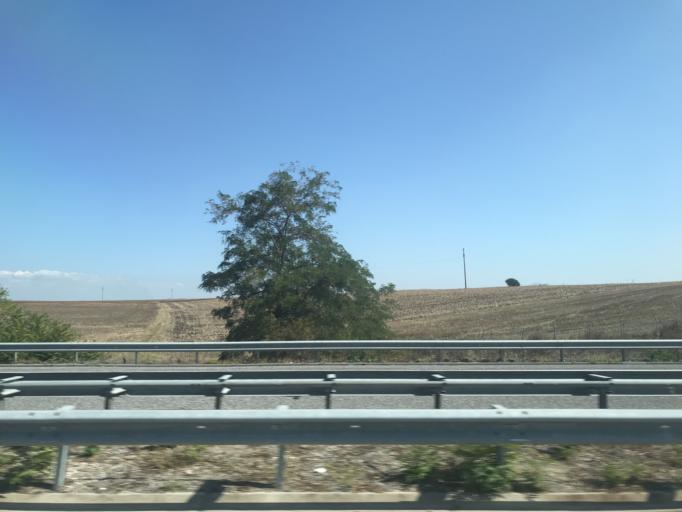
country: TR
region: Kirklareli
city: Luleburgaz
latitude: 41.4363
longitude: 27.3855
